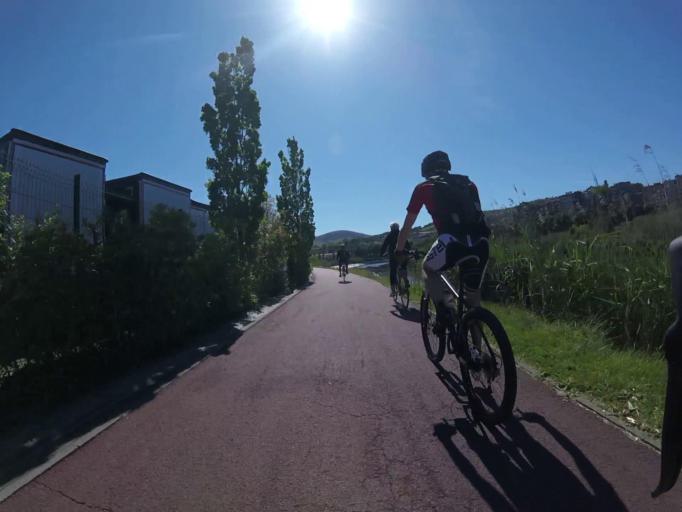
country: ES
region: Basque Country
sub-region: Provincia de Guipuzcoa
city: Irun
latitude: 43.3439
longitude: -1.7747
